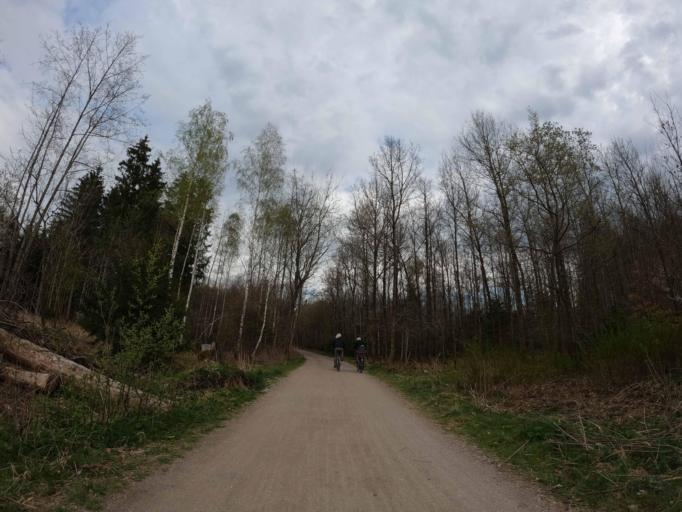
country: DE
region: Bavaria
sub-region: Upper Bavaria
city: Putzbrunn
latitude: 48.0981
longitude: 11.6921
